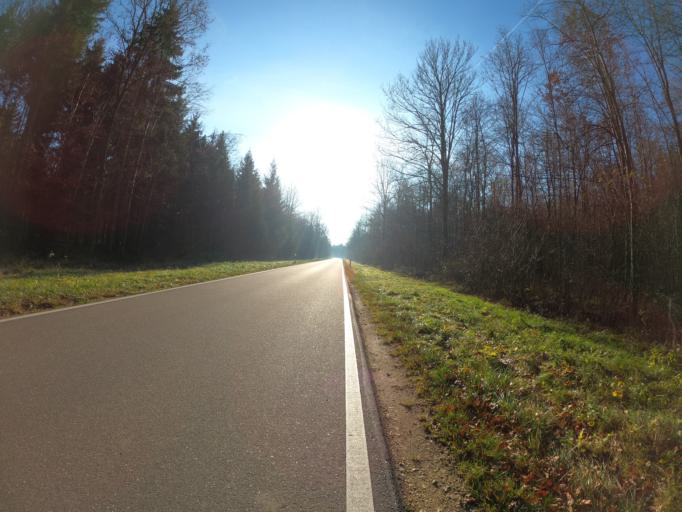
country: DE
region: Baden-Wuerttemberg
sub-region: Regierungsbezirk Stuttgart
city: Ebersbach an der Fils
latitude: 48.6951
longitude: 9.5376
